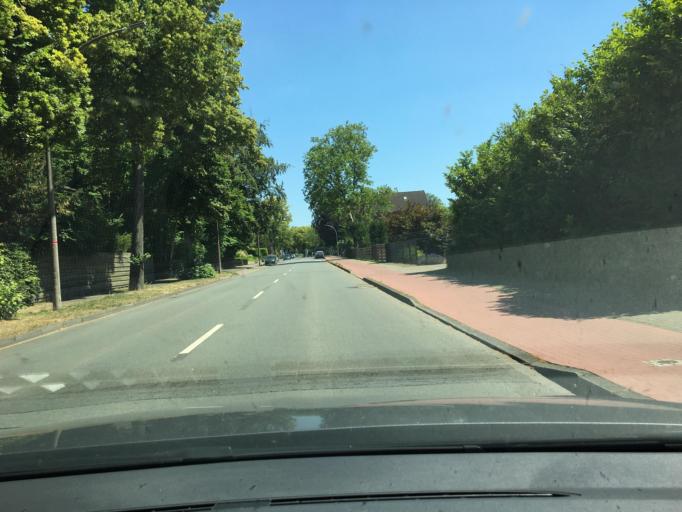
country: DE
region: North Rhine-Westphalia
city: Ahlen
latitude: 51.7731
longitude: 7.9007
